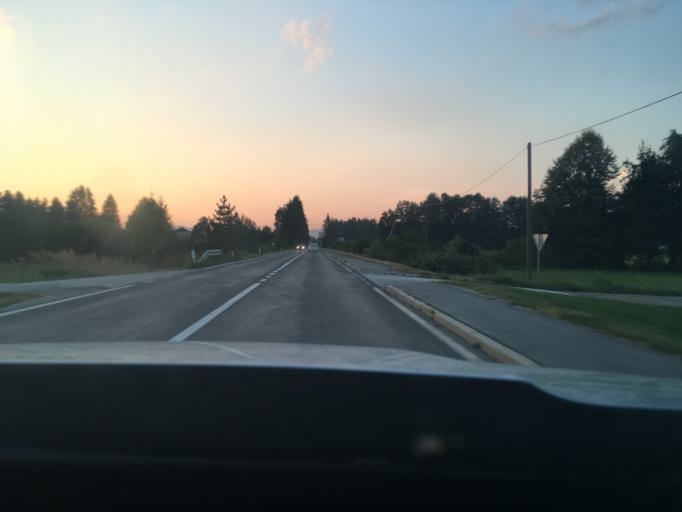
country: SI
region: Ribnica
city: Ribnica
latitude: 45.7246
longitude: 14.7405
